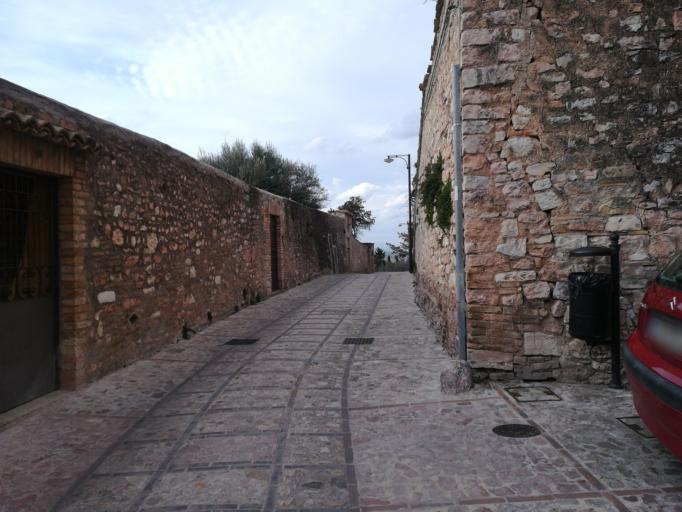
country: IT
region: Umbria
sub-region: Provincia di Perugia
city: Spello
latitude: 42.9939
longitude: 12.6707
